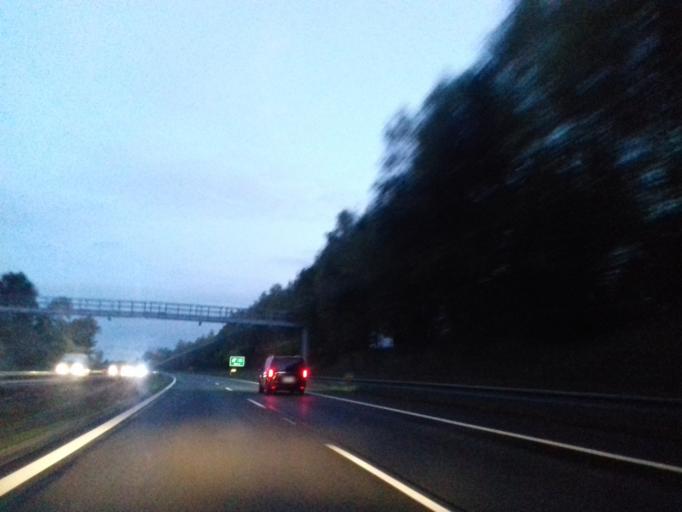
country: CZ
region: Vysocina
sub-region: Okres Pelhrimov
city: Humpolec
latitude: 49.5334
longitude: 15.3353
